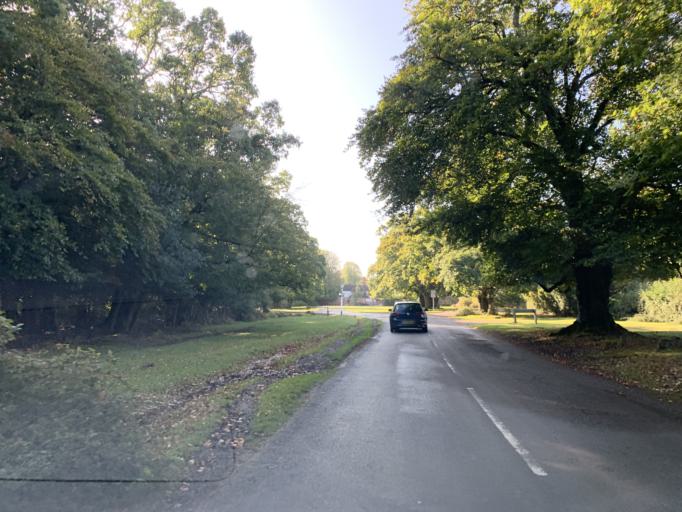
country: GB
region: England
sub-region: Hampshire
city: Cadnam
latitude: 50.9292
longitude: -1.6555
